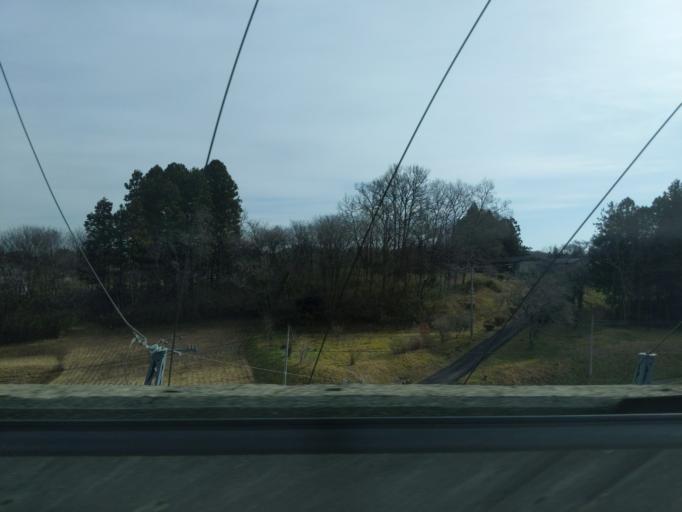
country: JP
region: Miyagi
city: Kogota
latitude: 38.7033
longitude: 141.0459
